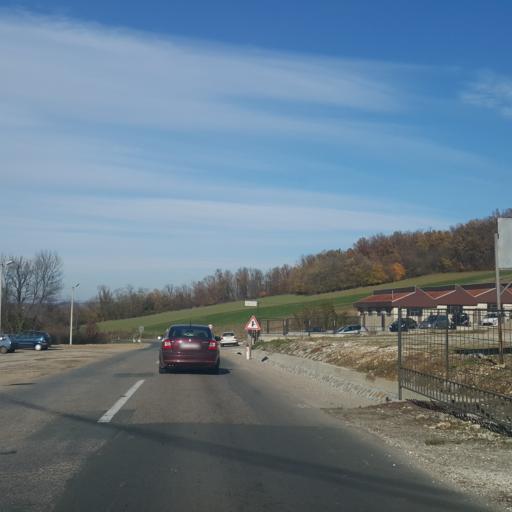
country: RS
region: Central Serbia
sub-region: Sumadijski Okrug
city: Topola
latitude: 44.2710
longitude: 20.6934
